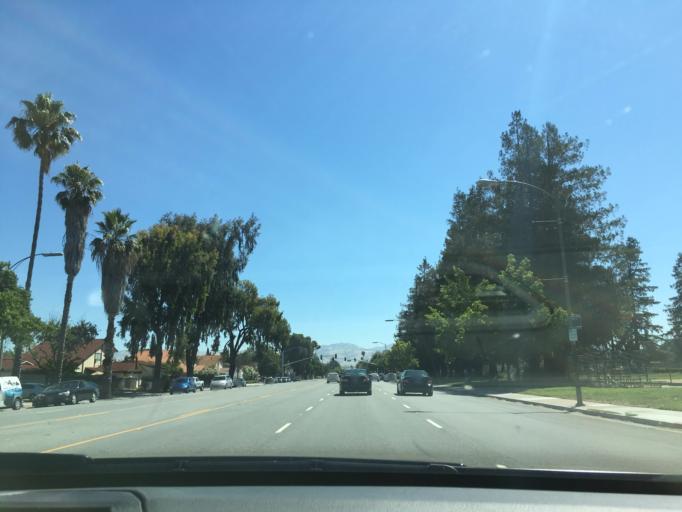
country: US
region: California
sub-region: Santa Clara County
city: Cambrian Park
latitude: 37.2719
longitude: -121.8916
